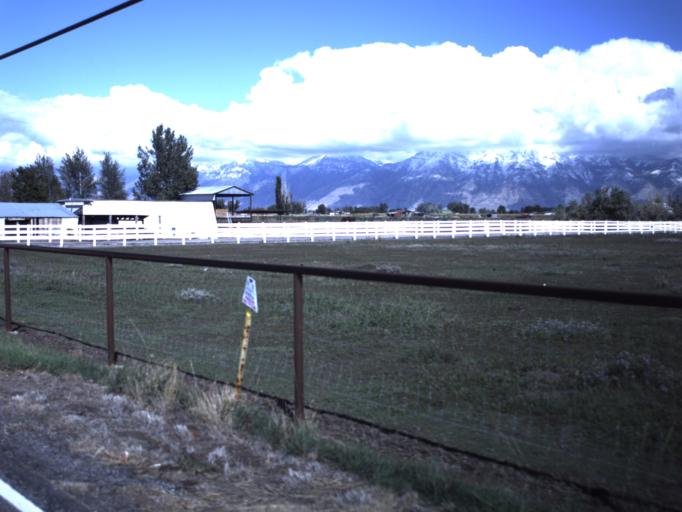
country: US
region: Utah
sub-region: Utah County
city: Benjamin
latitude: 40.1059
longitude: -111.7305
